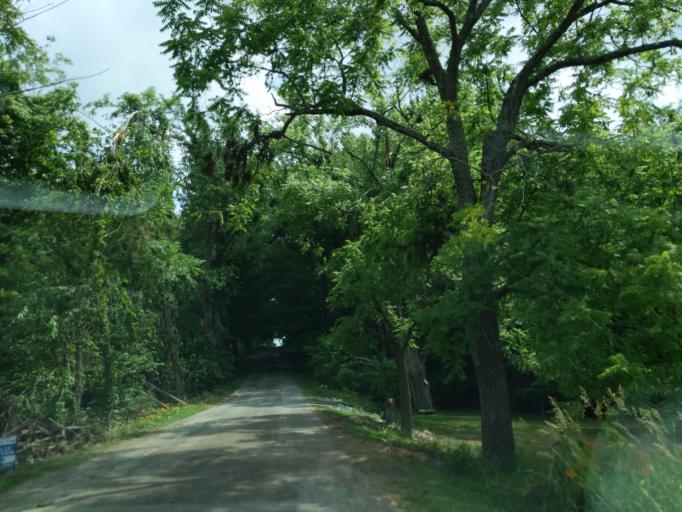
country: US
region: Indiana
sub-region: Ripley County
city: Batesville
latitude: 39.3288
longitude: -85.1899
